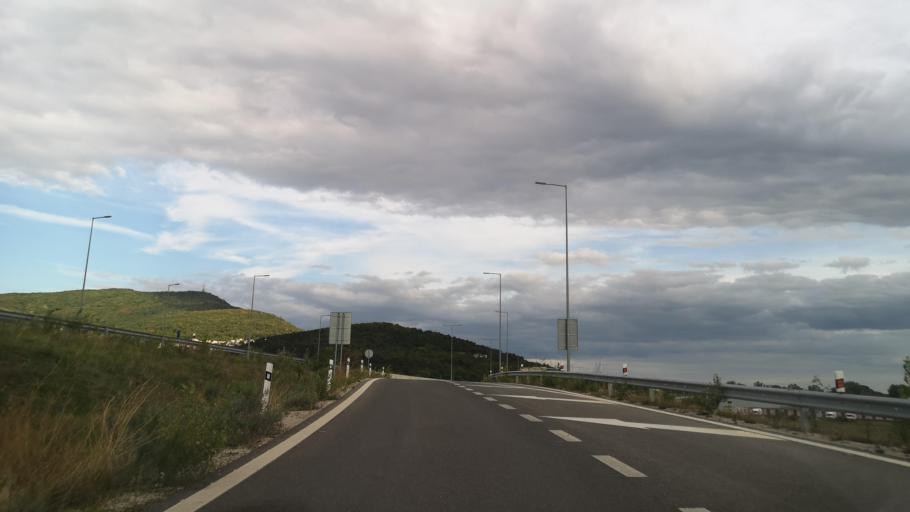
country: SK
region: Nitriansky
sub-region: Okres Nitra
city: Nitra
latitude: 48.3406
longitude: 18.0606
